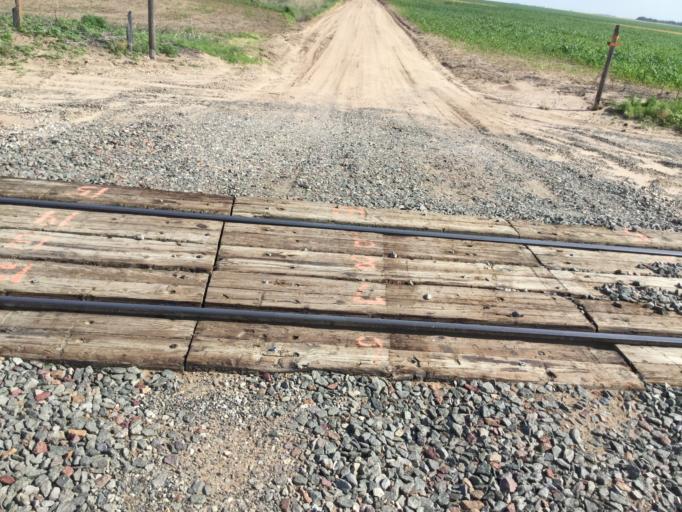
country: US
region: Kansas
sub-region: Pawnee County
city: Larned
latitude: 37.9546
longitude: -99.0772
